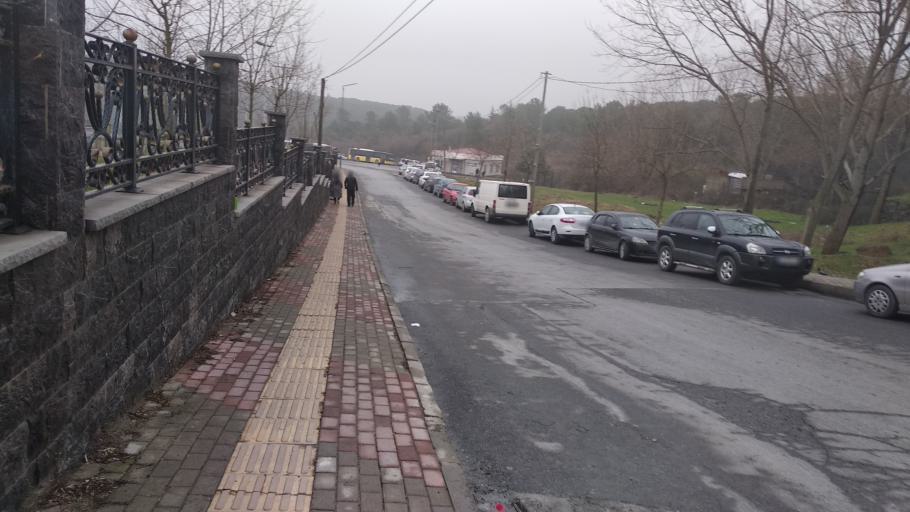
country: TR
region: Istanbul
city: Basaksehir
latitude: 41.1784
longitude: 28.7485
